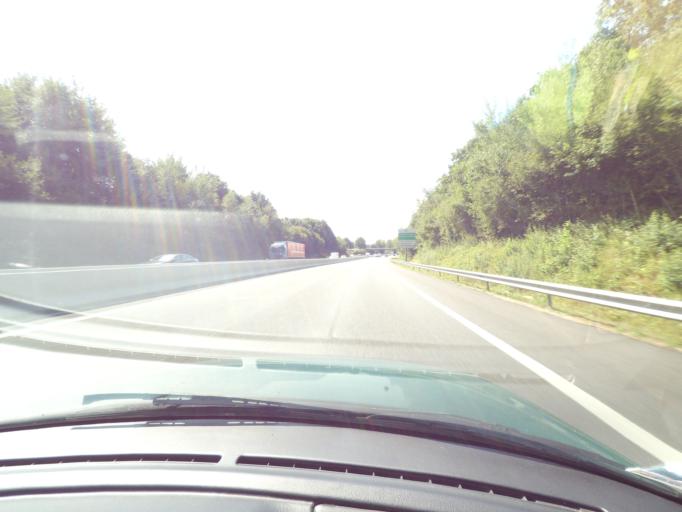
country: FR
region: Limousin
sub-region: Departement de la Haute-Vienne
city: Le Palais-sur-Vienne
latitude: 45.8633
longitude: 1.2872
